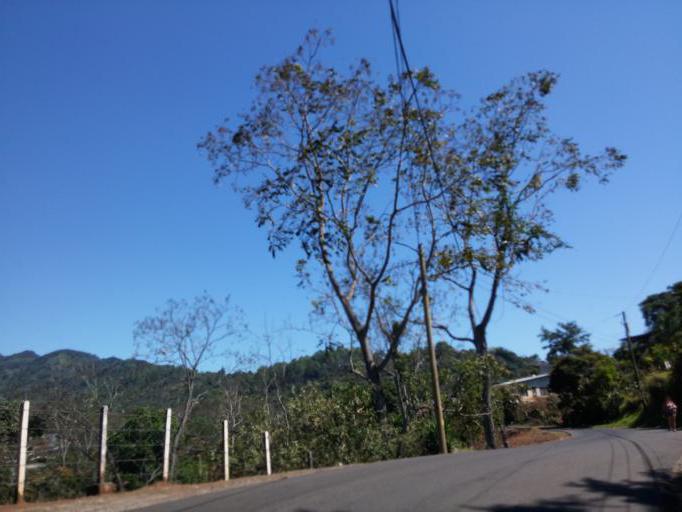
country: CR
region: San Jose
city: Palmichal
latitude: 9.8408
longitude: -84.2135
